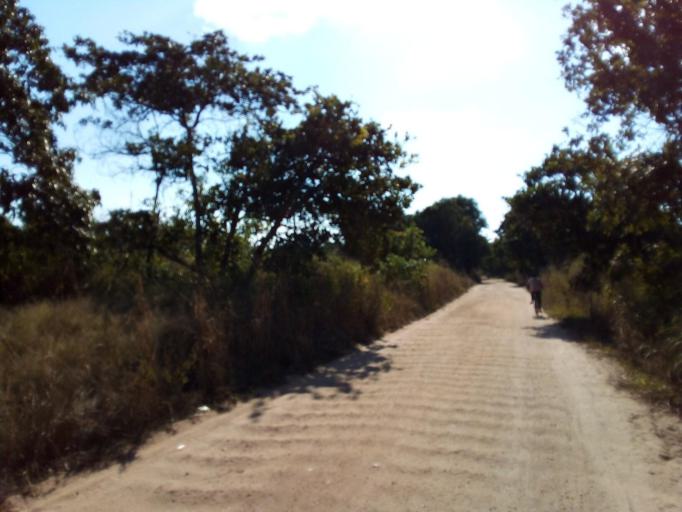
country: MZ
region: Zambezia
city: Quelimane
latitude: -17.5534
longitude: 36.6332
